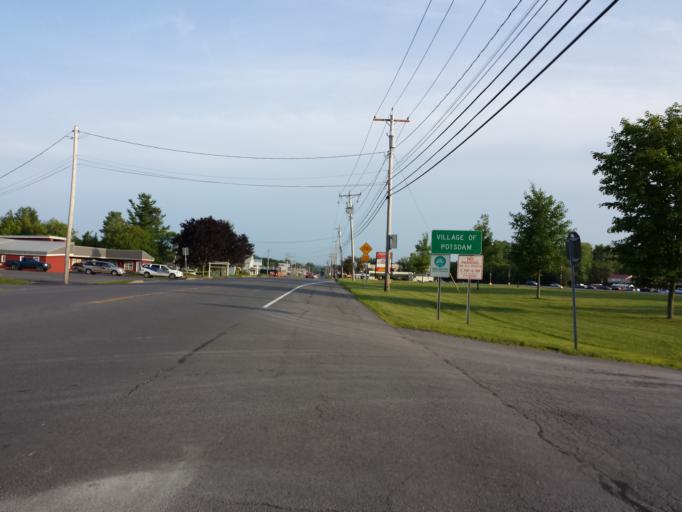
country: US
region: New York
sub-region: St. Lawrence County
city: Potsdam
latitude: 44.6877
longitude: -74.9871
